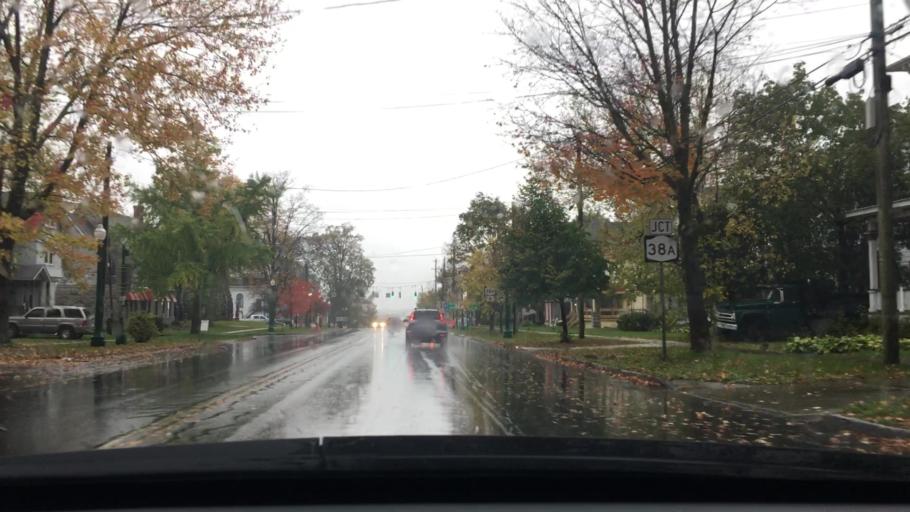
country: US
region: New York
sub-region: Cayuga County
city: Auburn
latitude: 42.9334
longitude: -76.5571
